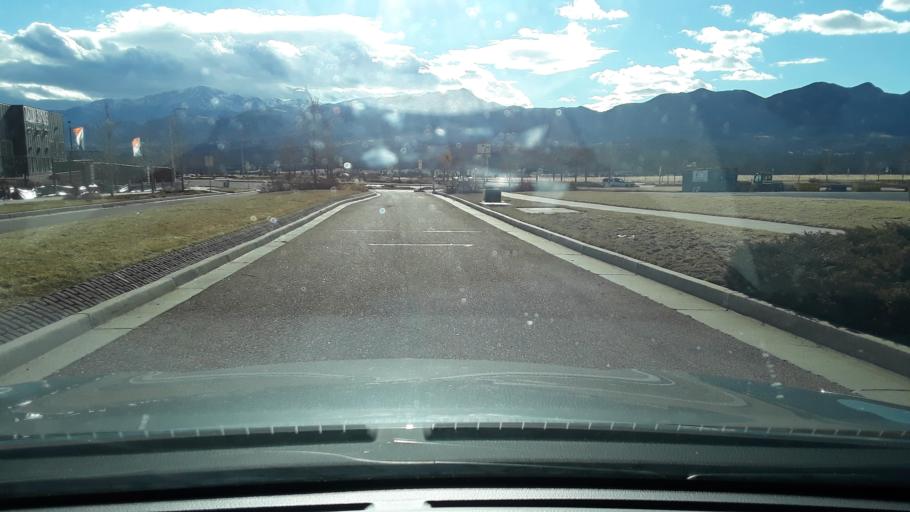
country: US
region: Colorado
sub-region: El Paso County
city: Air Force Academy
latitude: 38.9872
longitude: -104.8059
